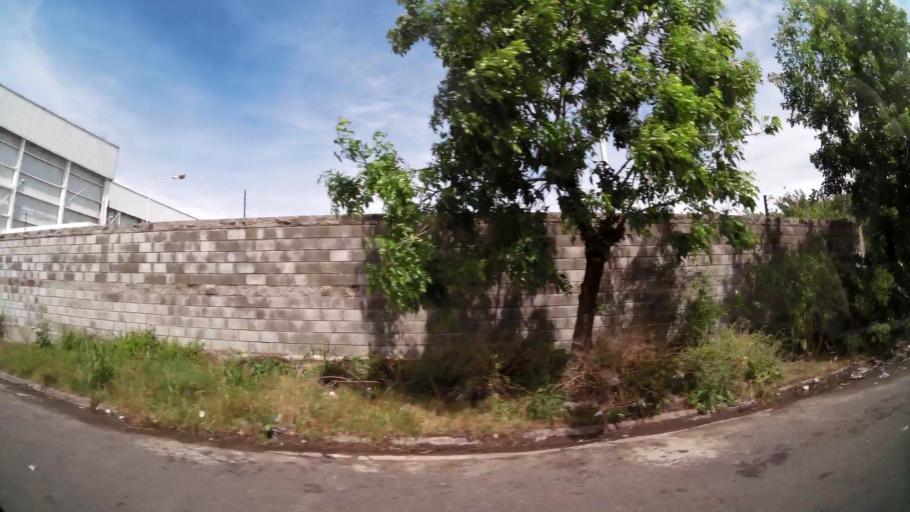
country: AR
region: Buenos Aires F.D.
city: Villa Lugano
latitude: -34.6662
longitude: -58.4362
